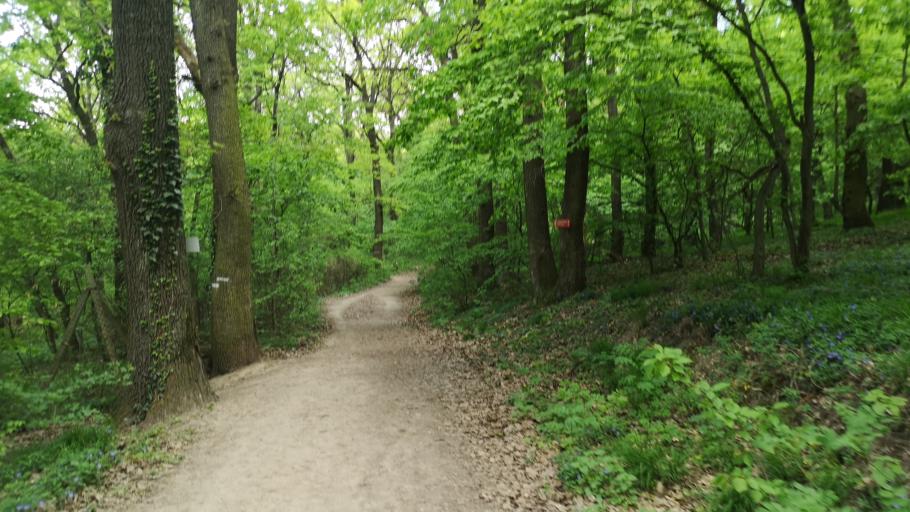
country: SK
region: Nitriansky
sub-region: Okres Nitra
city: Nitra
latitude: 48.3439
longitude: 18.0925
